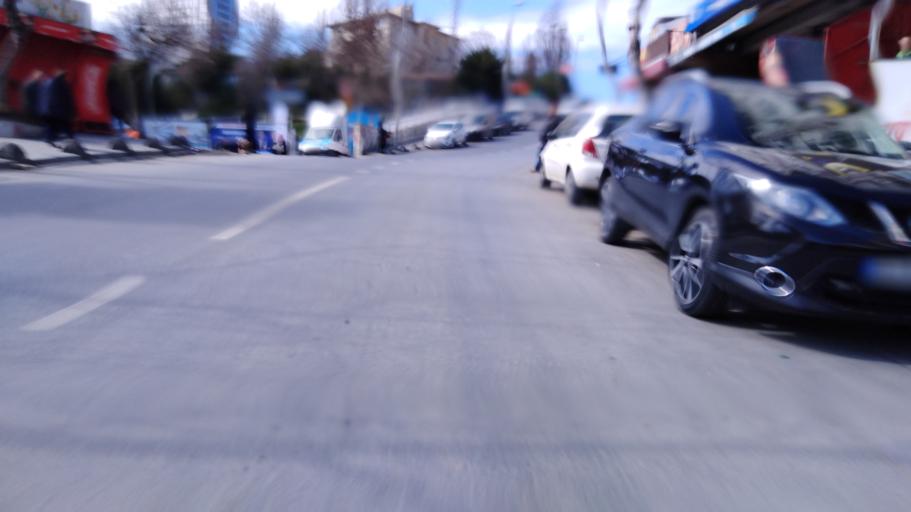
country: TR
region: Istanbul
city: Esenler
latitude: 41.0492
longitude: 28.8968
